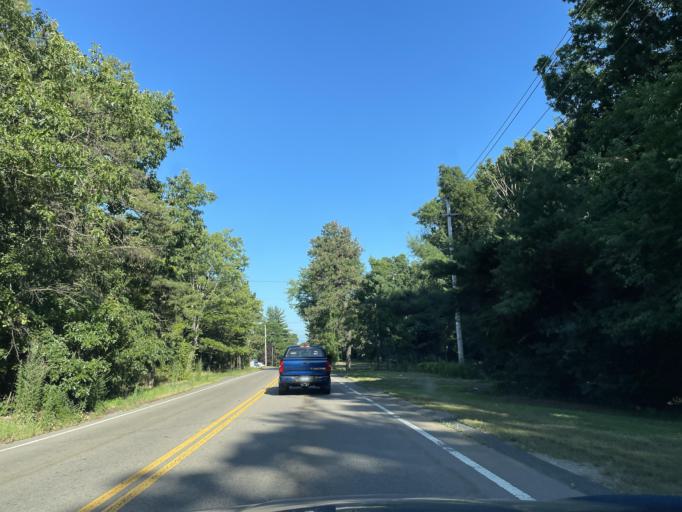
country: US
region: Massachusetts
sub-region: Norfolk County
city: Franklin
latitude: 42.0750
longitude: -71.3630
